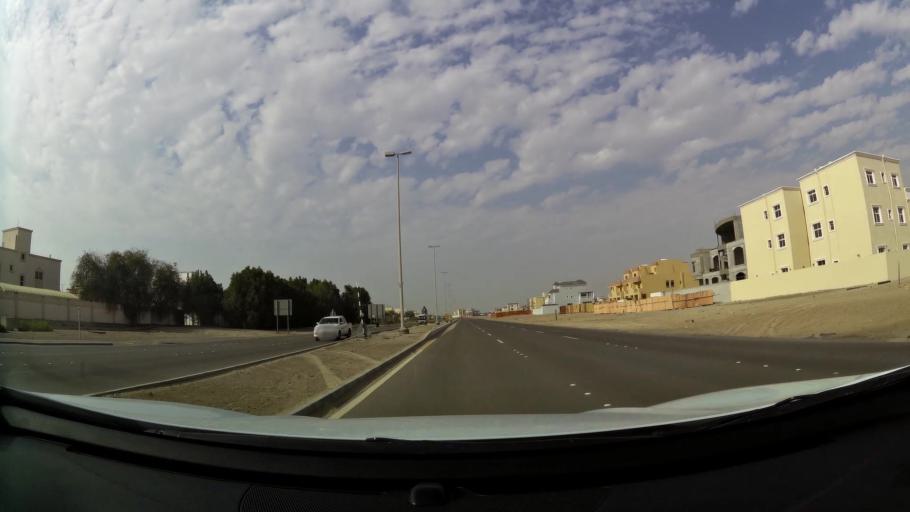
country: AE
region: Abu Dhabi
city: Abu Dhabi
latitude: 24.3273
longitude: 54.5743
